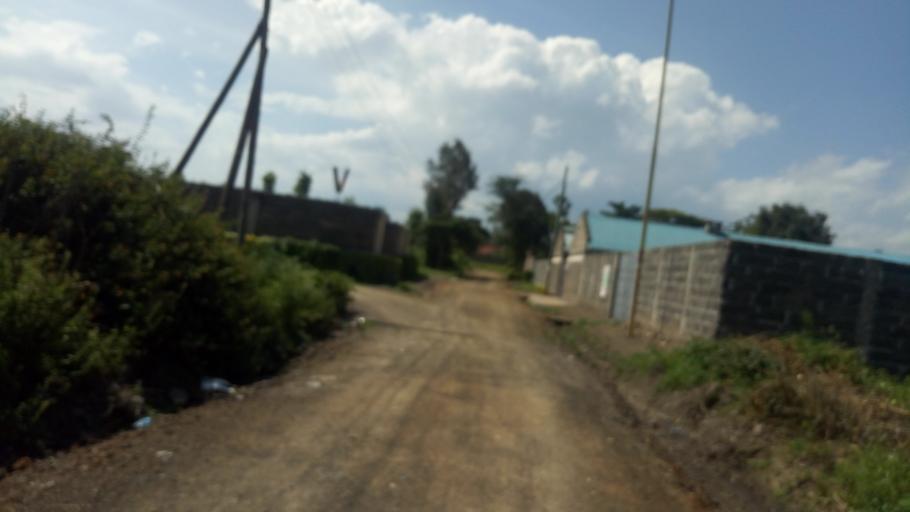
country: KE
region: Nakuru
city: Nakuru
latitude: -0.2771
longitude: 36.1194
